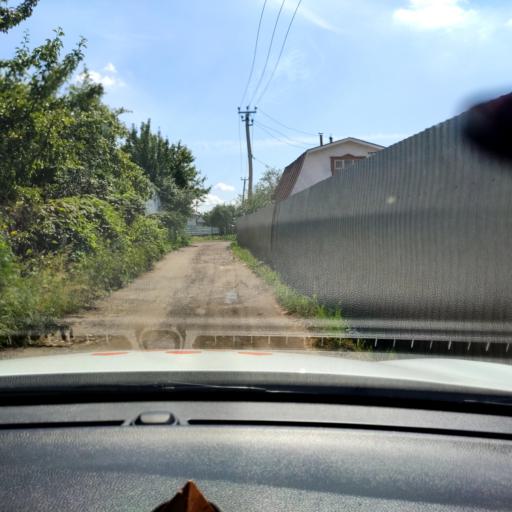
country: RU
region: Tatarstan
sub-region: Gorod Kazan'
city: Kazan
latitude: 55.8335
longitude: 49.2225
